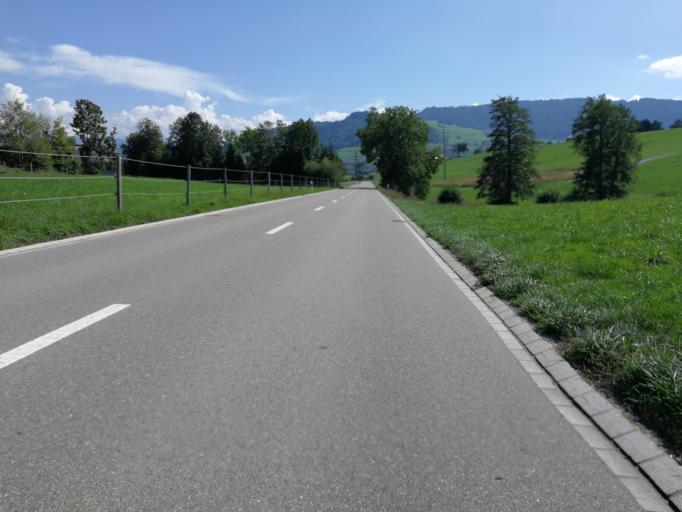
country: CH
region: Zurich
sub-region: Bezirk Horgen
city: Waedenswil / Eichweid
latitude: 47.2014
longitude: 8.6709
